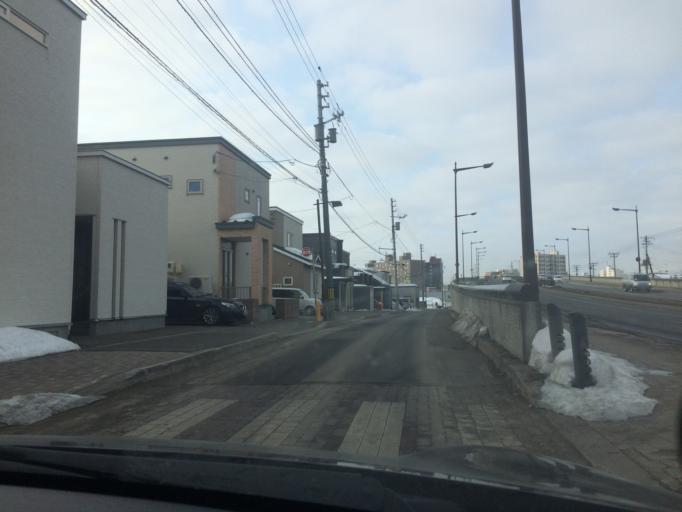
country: JP
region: Hokkaido
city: Ebetsu
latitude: 43.0503
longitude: 141.4718
